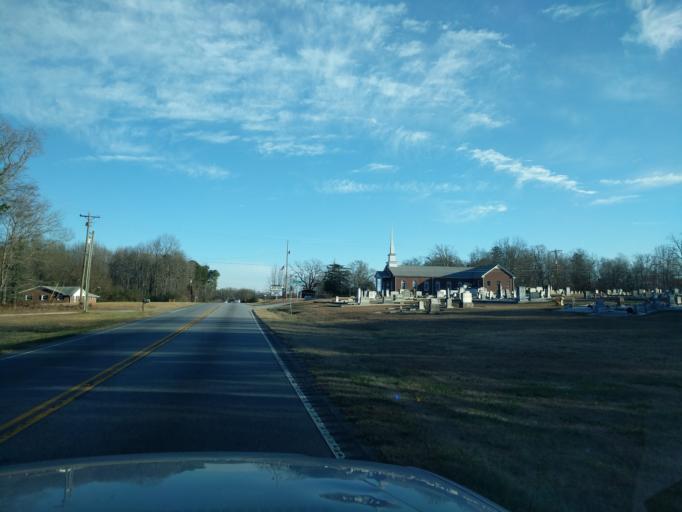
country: US
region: South Carolina
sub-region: Anderson County
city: Piedmont
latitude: 34.6708
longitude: -82.5275
